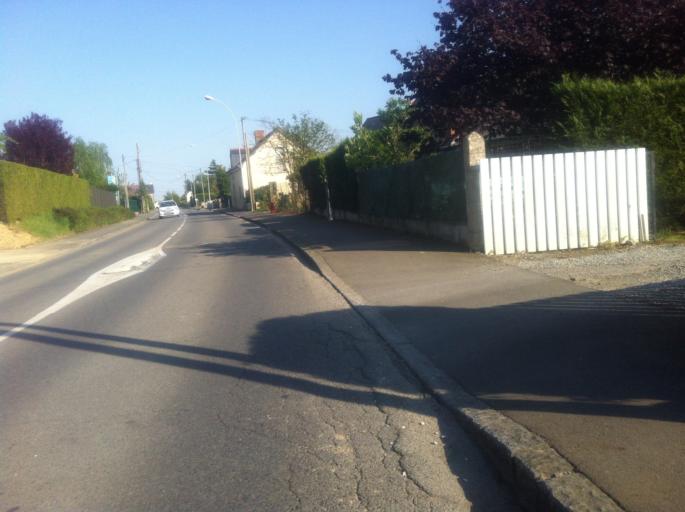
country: FR
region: Brittany
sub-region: Departement d'Ille-et-Vilaine
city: Bruz
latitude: 48.0219
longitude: -1.7332
